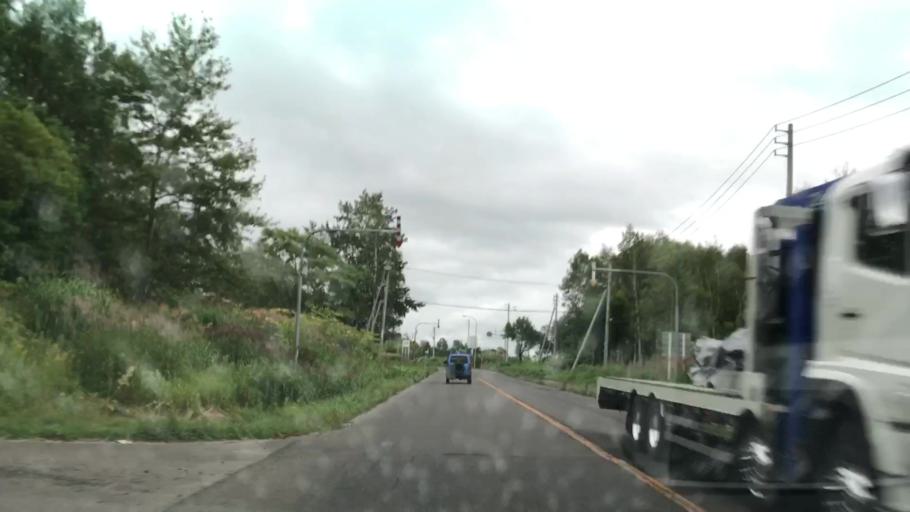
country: JP
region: Hokkaido
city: Niseko Town
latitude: 42.7954
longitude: 140.7519
